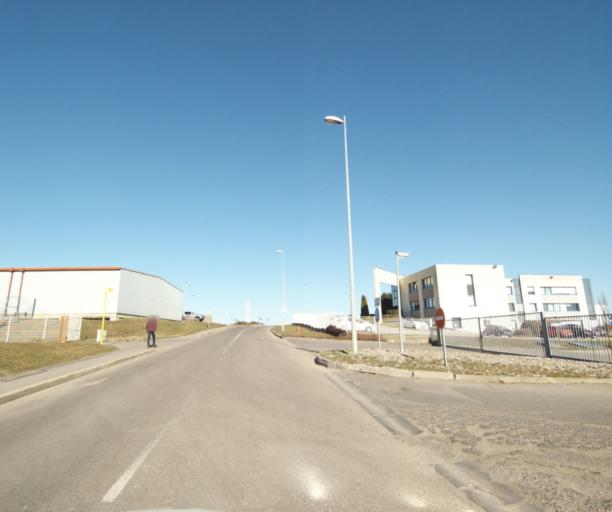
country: FR
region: Lorraine
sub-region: Departement de Meurthe-et-Moselle
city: Fleville-devant-Nancy
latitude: 48.6162
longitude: 6.2099
